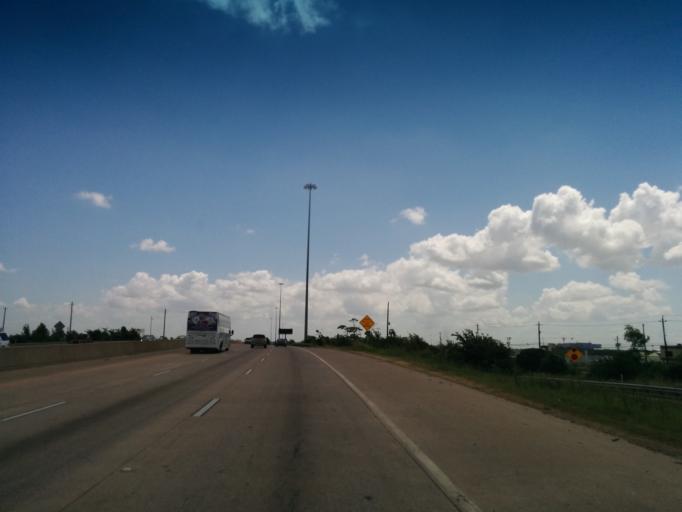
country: US
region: Texas
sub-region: Harris County
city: Channelview
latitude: 29.7915
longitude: -95.0818
